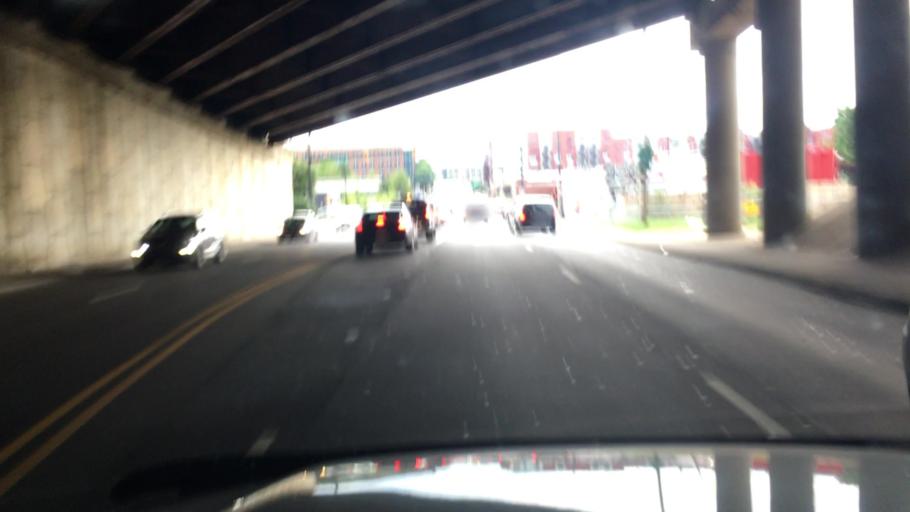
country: US
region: North Carolina
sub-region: Mecklenburg County
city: Charlotte
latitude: 35.2243
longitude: -80.8546
